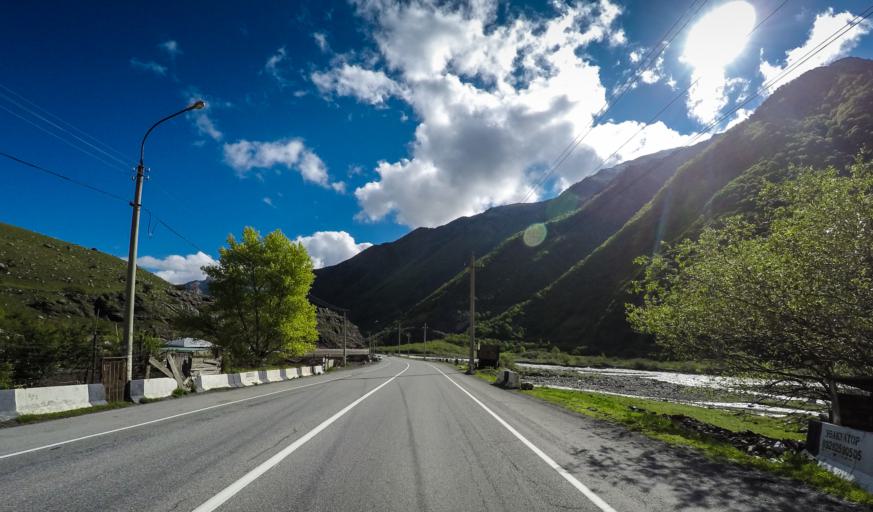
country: RU
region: Ingushetiya
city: Dzhayrakh
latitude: 42.7955
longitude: 44.6354
